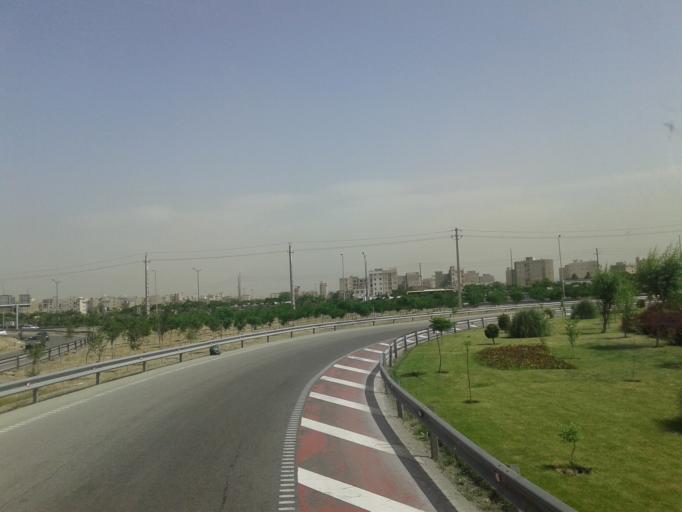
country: IR
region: Tehran
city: Eslamshahr
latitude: 35.6497
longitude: 51.2710
